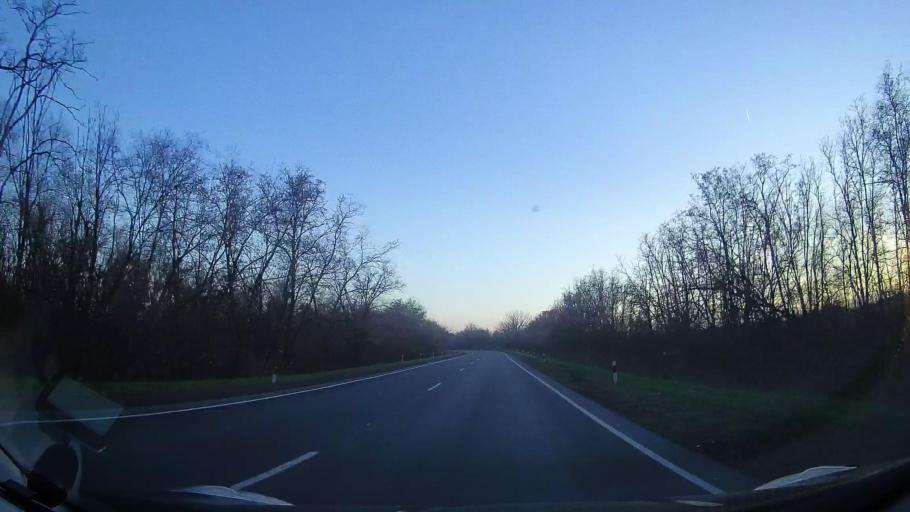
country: RU
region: Rostov
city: Bagayevskaya
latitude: 47.1030
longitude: 40.2767
